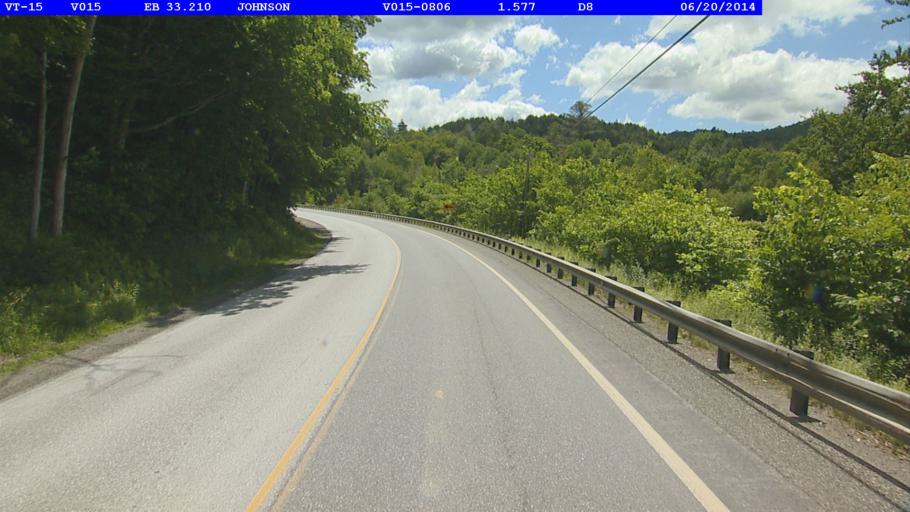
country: US
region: Vermont
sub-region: Lamoille County
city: Johnson
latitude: 44.6427
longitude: -72.7251
